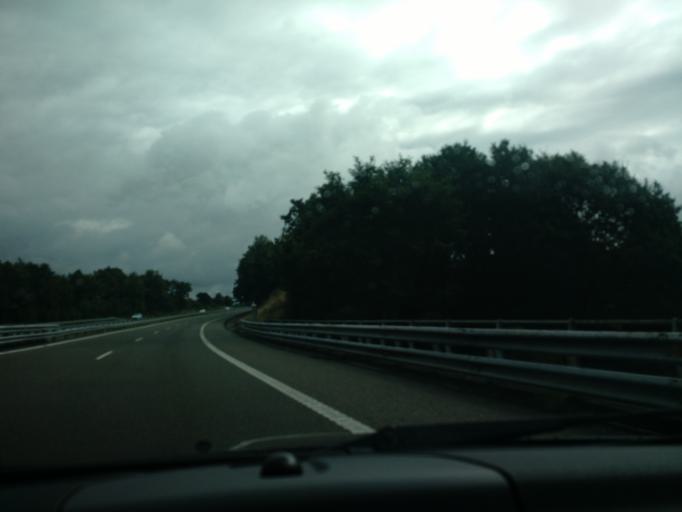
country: ES
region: Galicia
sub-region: Provincia da Coruna
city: Oroso
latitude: 42.9714
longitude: -8.4510
